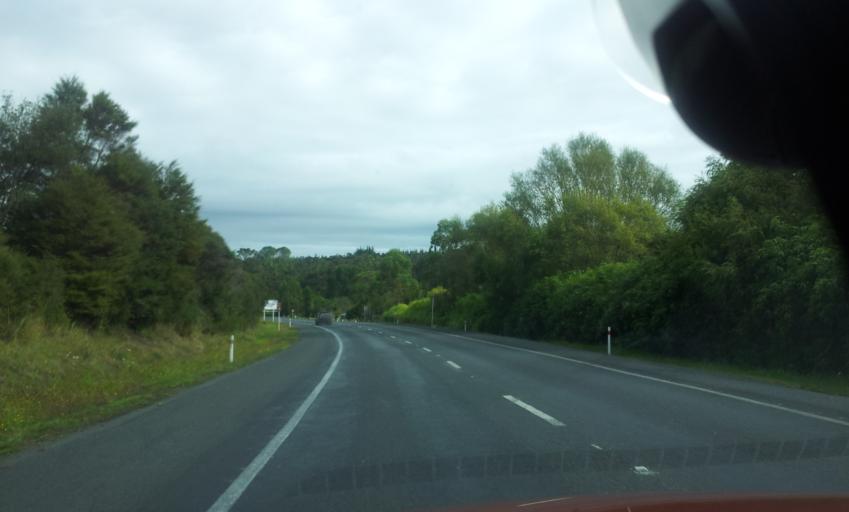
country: NZ
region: Auckland
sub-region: Auckland
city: Warkworth
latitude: -36.3510
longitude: 174.5944
